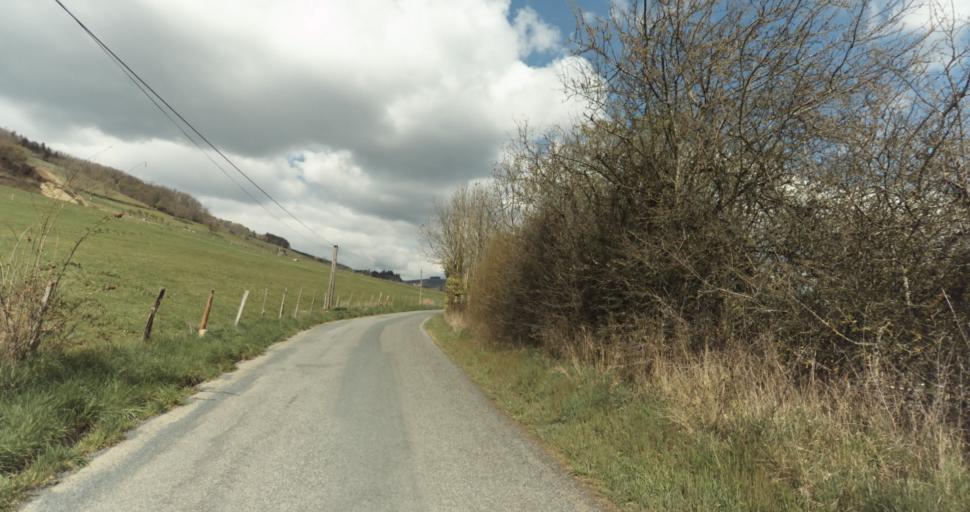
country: FR
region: Rhone-Alpes
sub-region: Departement du Rhone
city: Tarare
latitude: 45.9074
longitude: 4.4271
